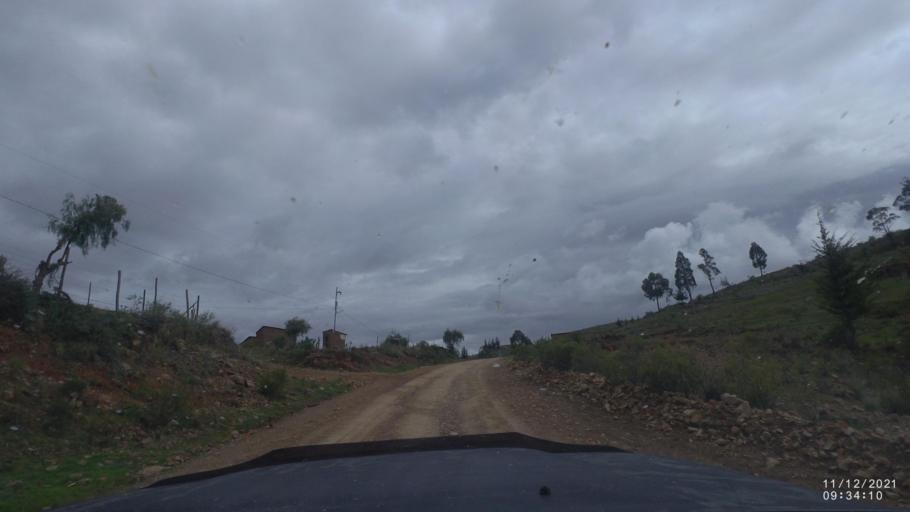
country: BO
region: Cochabamba
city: Tarata
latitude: -17.8346
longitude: -65.9920
